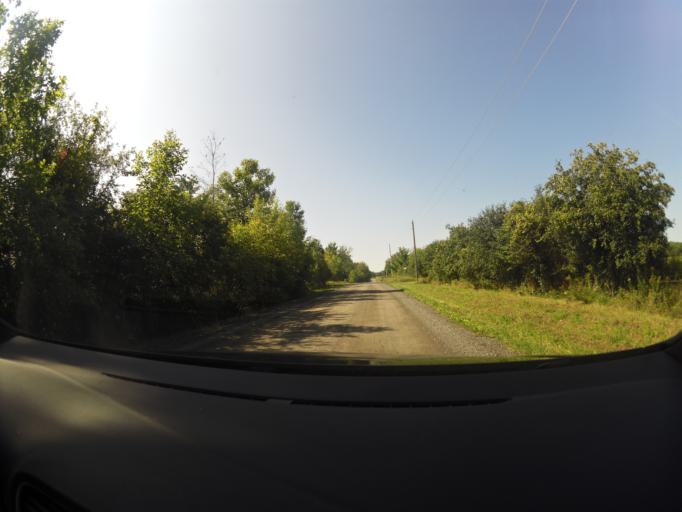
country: CA
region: Ontario
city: Arnprior
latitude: 45.3479
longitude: -76.2712
